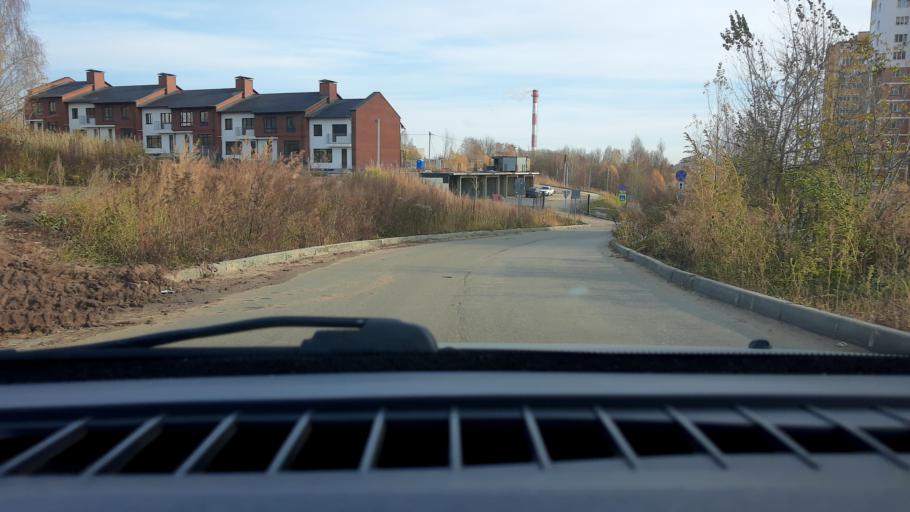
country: RU
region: Nizjnij Novgorod
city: Afonino
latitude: 56.2854
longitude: 44.0888
